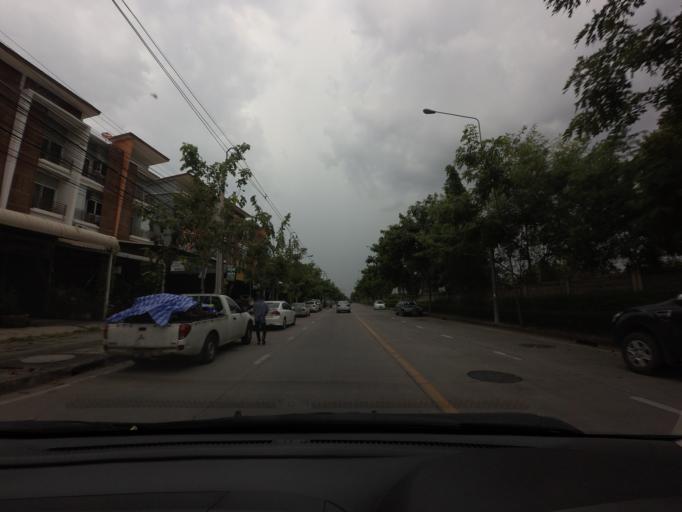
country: TH
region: Bangkok
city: Don Mueang
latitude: 13.9449
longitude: 100.5829
